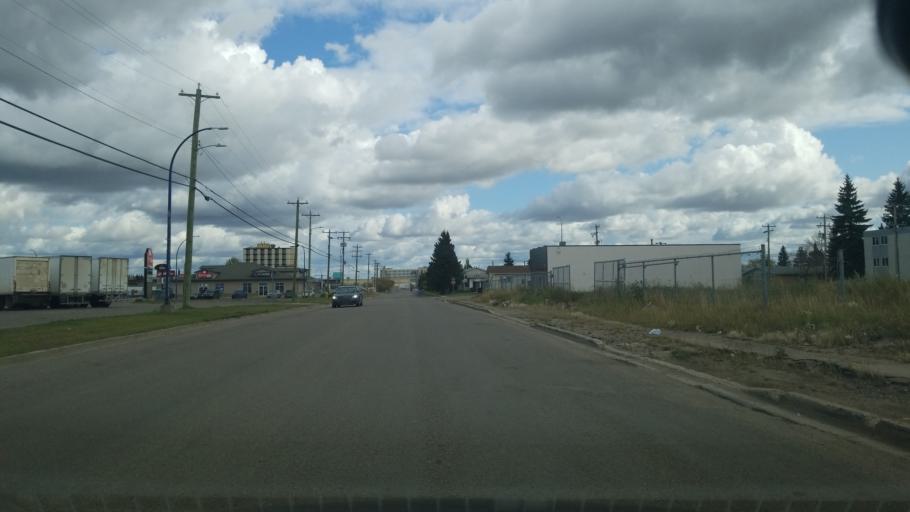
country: CA
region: Saskatchewan
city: Lloydminster
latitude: 53.2769
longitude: -110.0269
